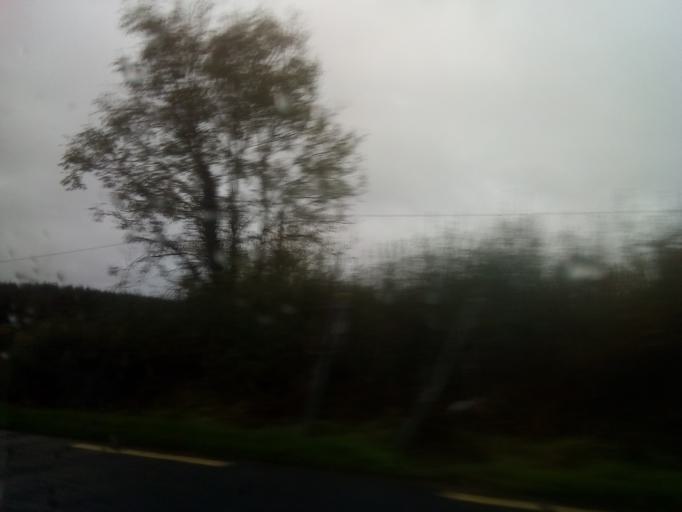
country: IE
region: Connaught
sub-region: Roscommon
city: Castlerea
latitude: 53.8521
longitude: -8.3906
